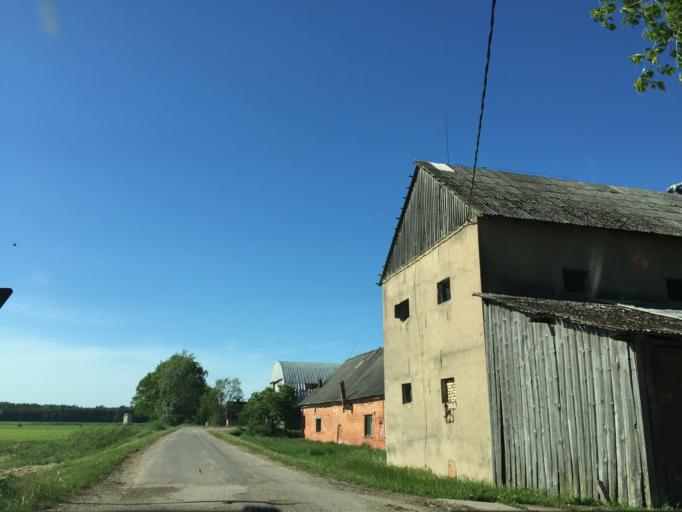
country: LV
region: Jelgava
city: Jelgava
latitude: 56.5429
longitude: 23.7222
